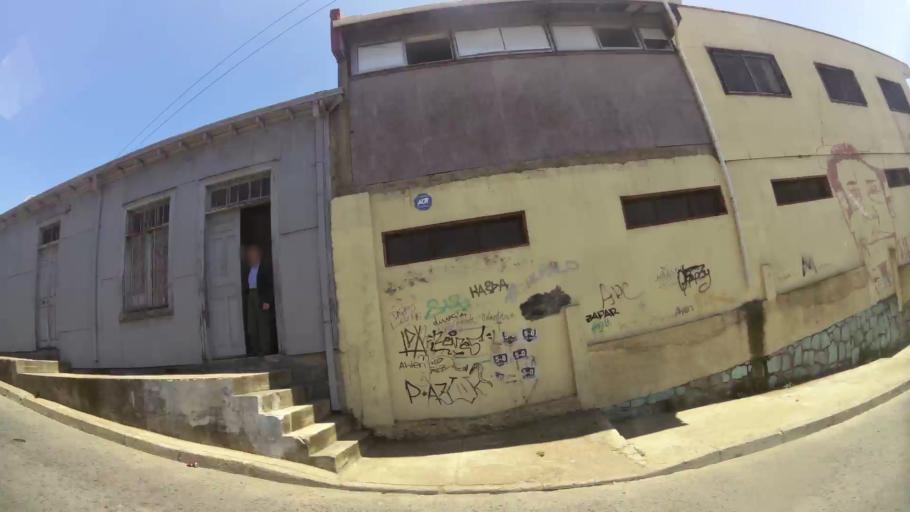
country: CL
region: Valparaiso
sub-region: Provincia de Valparaiso
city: Valparaiso
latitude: -33.0348
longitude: -71.6412
